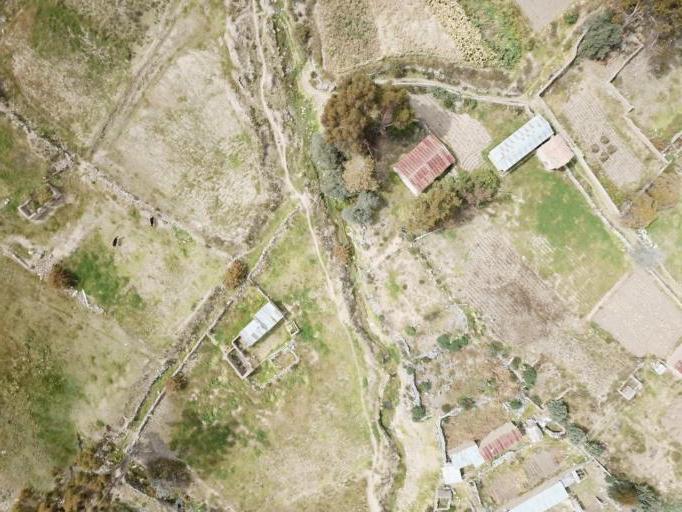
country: BO
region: La Paz
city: Achacachi
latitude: -16.0518
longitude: -68.8136
